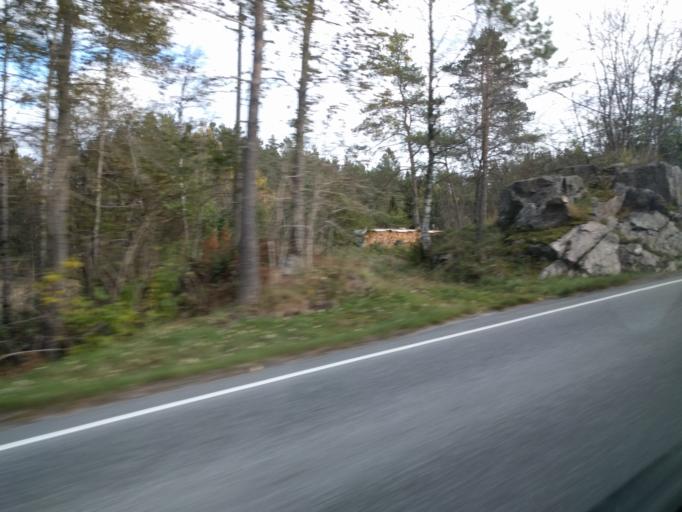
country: NO
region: Vest-Agder
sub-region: Songdalen
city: Nodeland
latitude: 58.2537
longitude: 7.8463
